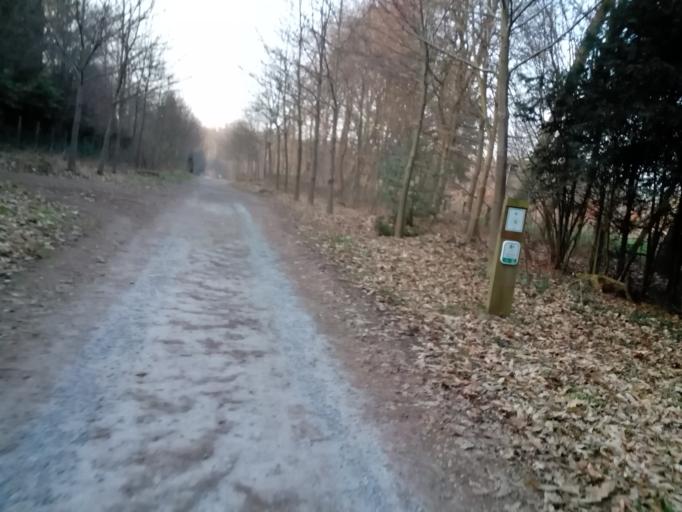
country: BE
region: Flanders
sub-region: Provincie Vlaams-Brabant
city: Oud-Heverlee
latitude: 50.8310
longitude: 4.6944
